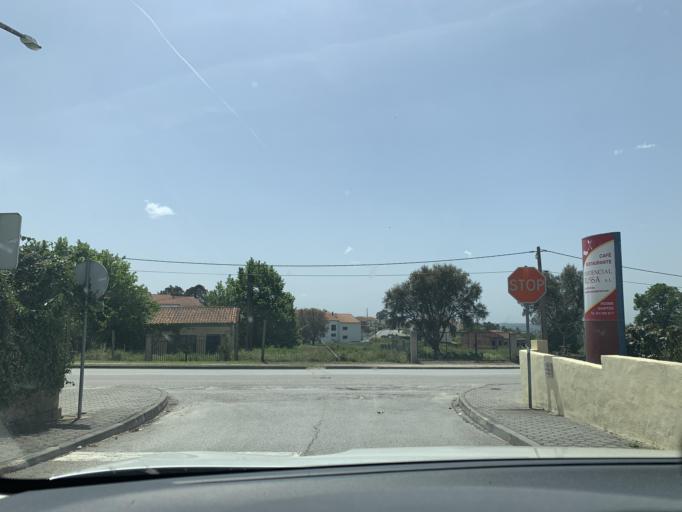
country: PT
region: Viseu
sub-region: Mangualde
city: Mangualde
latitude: 40.6053
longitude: -7.7740
